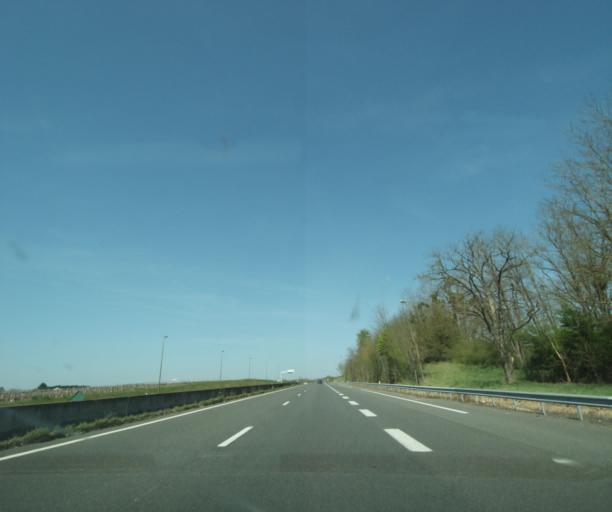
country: FR
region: Bourgogne
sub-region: Departement de la Nievre
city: Pouilly-sur-Loire
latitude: 47.2749
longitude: 2.9762
